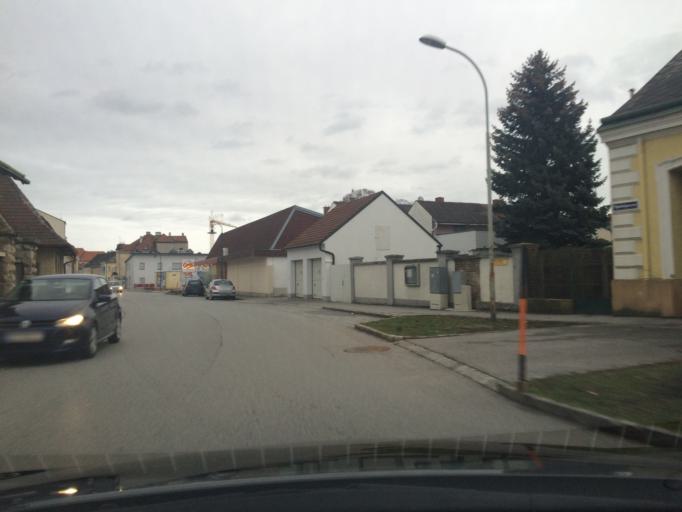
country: AT
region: Lower Austria
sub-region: Politischer Bezirk Ganserndorf
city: Zistersdorf
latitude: 48.5459
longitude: 16.7574
